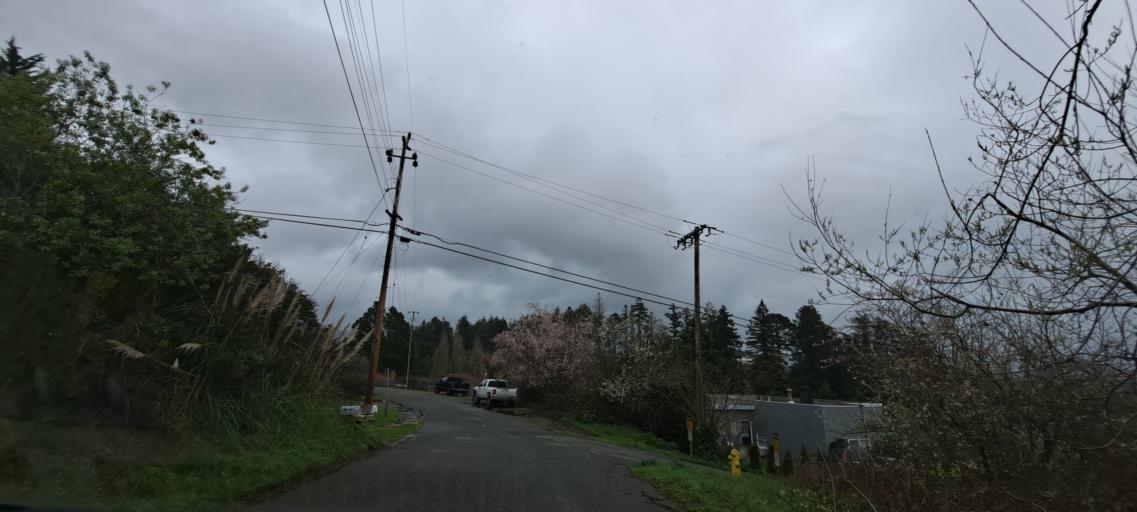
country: US
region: California
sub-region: Humboldt County
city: Fortuna
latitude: 40.5982
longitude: -124.1448
